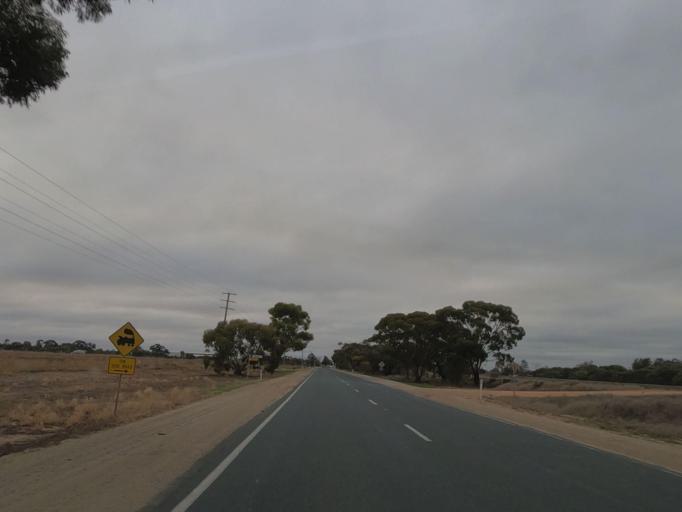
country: AU
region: Victoria
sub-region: Swan Hill
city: Swan Hill
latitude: -35.3933
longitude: 143.5715
